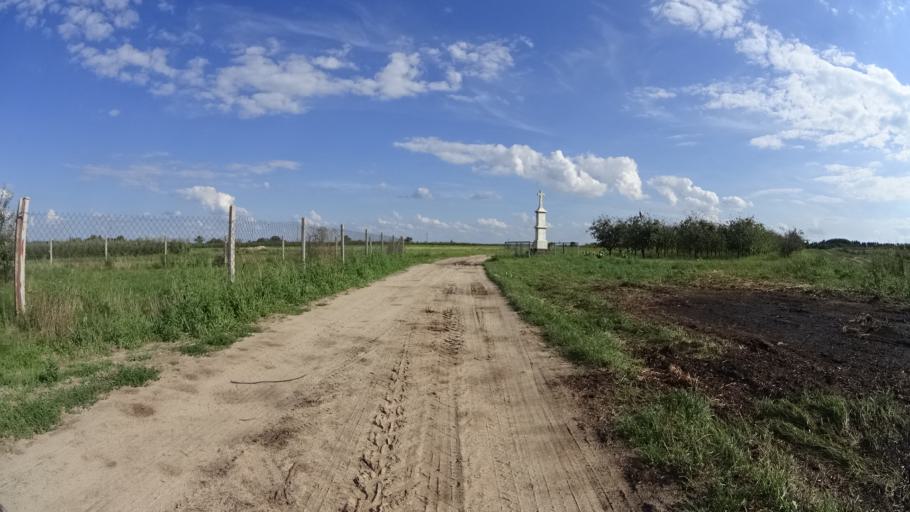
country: PL
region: Masovian Voivodeship
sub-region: Powiat bialobrzeski
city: Wysmierzyce
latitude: 51.6611
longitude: 20.8195
